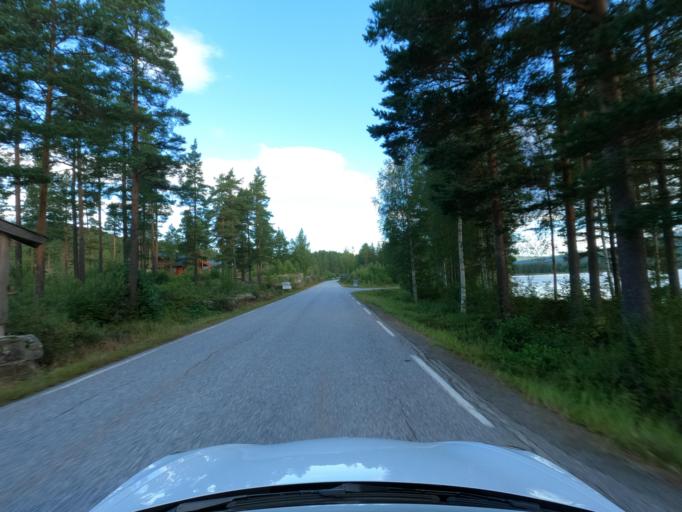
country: NO
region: Telemark
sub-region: Hjartdal
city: Sauland
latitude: 59.8028
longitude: 9.0854
